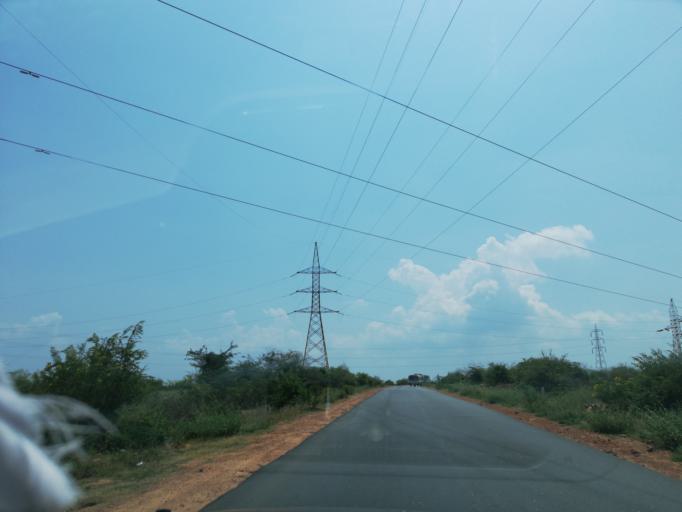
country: IN
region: Andhra Pradesh
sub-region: Guntur
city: Macherla
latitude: 16.5681
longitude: 79.3456
